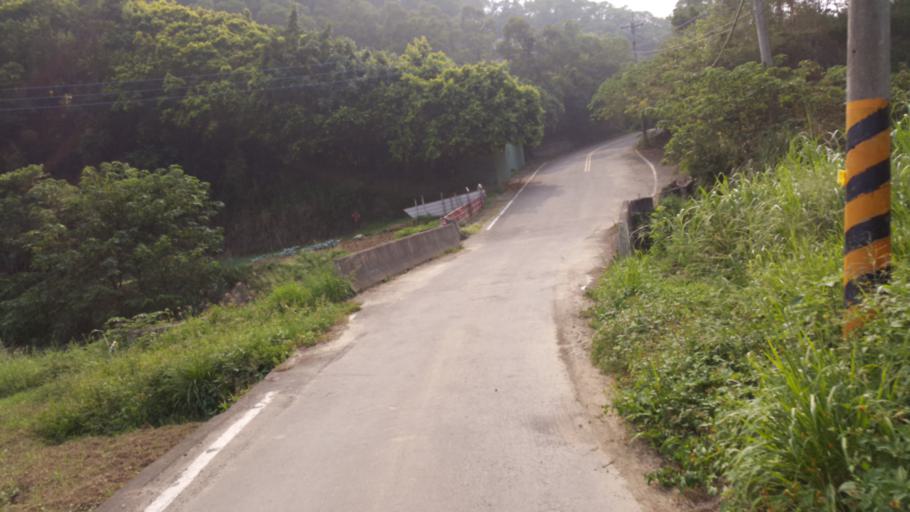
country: TW
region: Taiwan
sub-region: Hsinchu
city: Hsinchu
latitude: 24.7226
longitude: 120.9580
